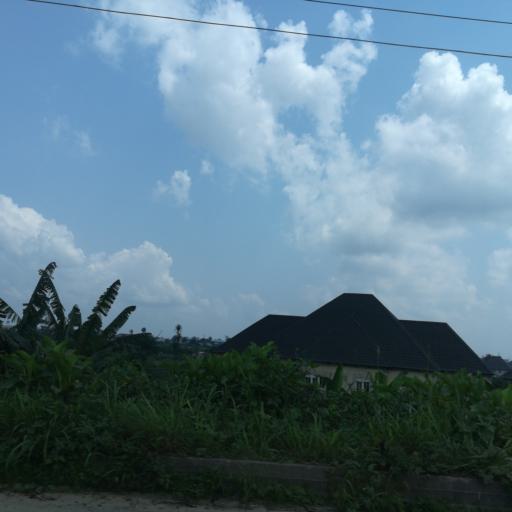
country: NG
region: Rivers
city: Port Harcourt
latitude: 4.8430
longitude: 7.0792
